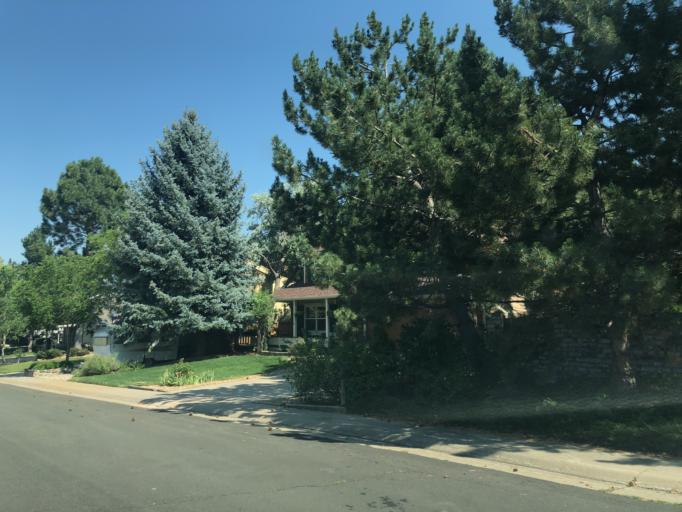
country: US
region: Colorado
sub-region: Arapahoe County
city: Dove Valley
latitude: 39.6350
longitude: -104.7697
